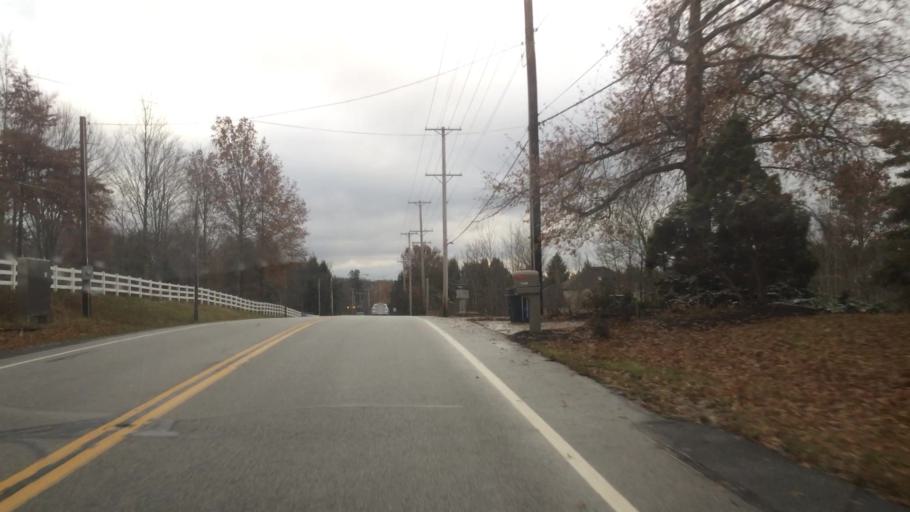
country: US
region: Ohio
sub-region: Summit County
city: Hudson
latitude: 41.2070
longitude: -81.4114
